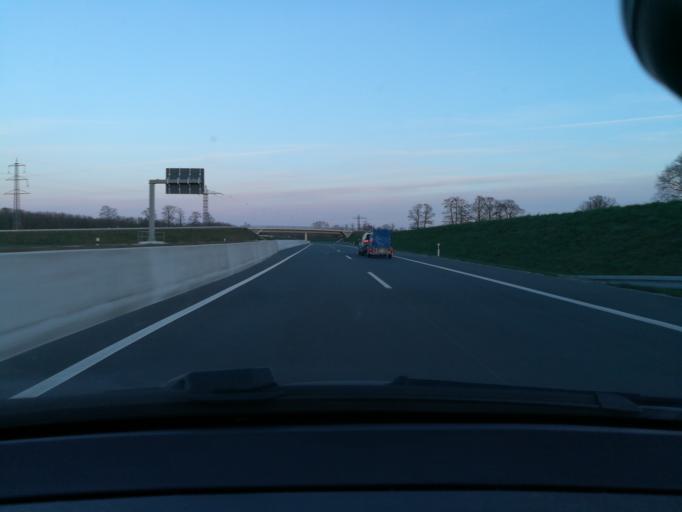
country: DE
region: North Rhine-Westphalia
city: Halle
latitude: 52.0354
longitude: 8.3472
